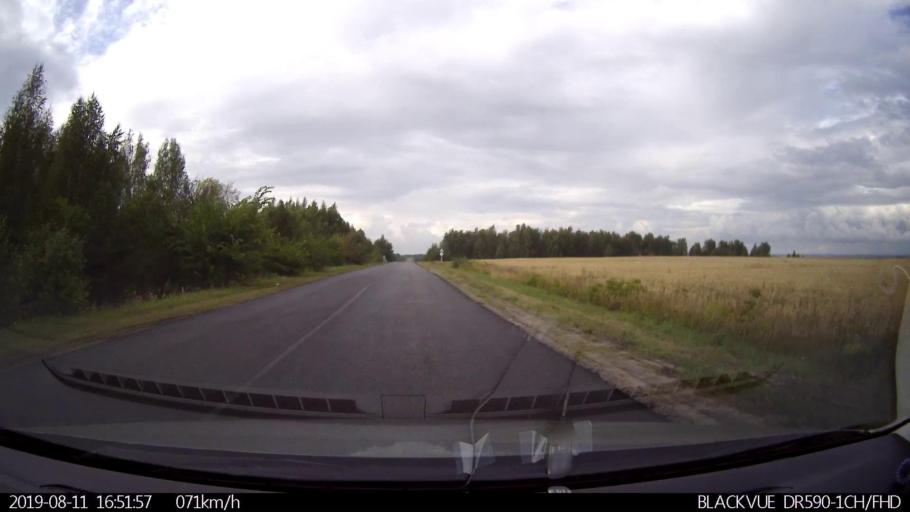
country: RU
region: Ulyanovsk
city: Mayna
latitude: 54.2425
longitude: 47.6756
